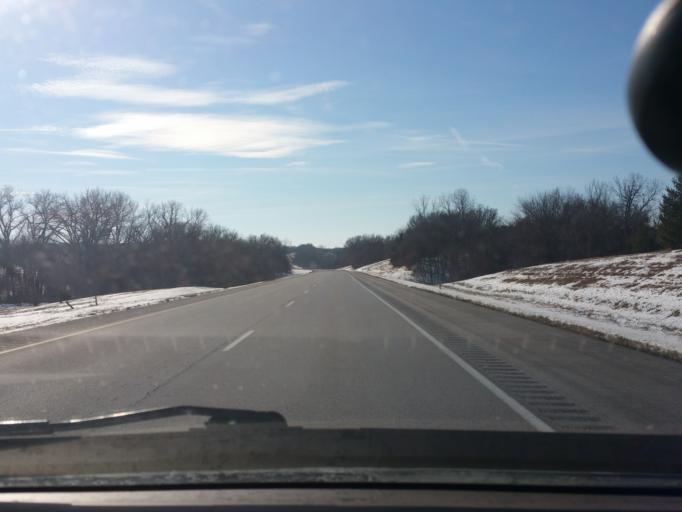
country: US
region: Iowa
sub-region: Decatur County
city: Leon
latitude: 40.7193
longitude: -93.8444
